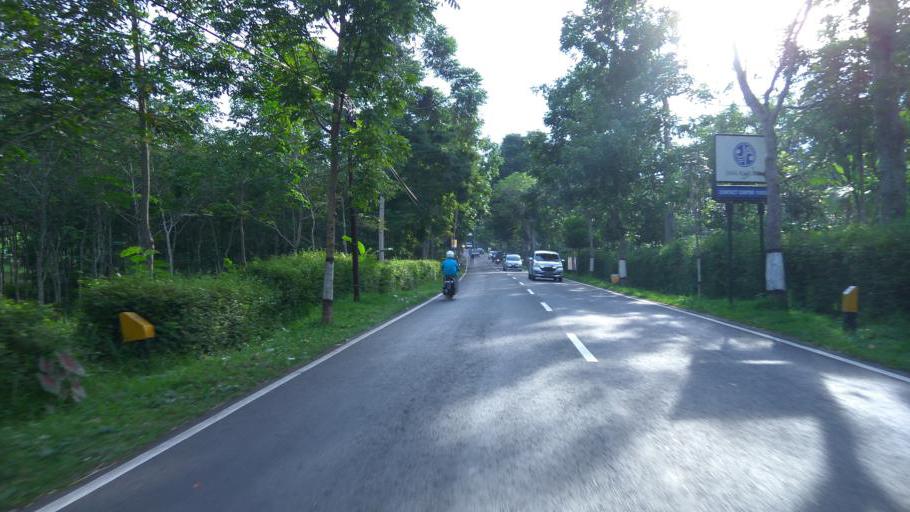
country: ID
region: Central Java
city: Salatiga
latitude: -7.3578
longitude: 110.4812
